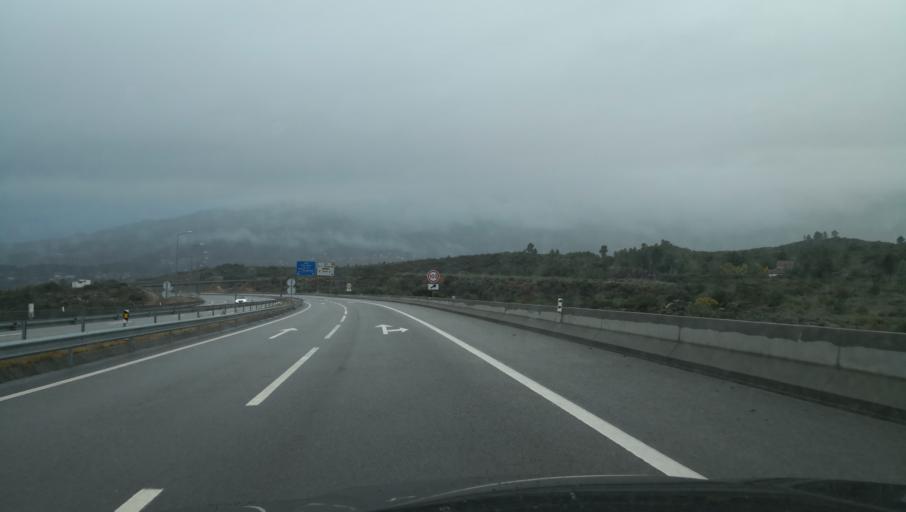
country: PT
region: Vila Real
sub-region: Vila Real
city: Vila Real
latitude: 41.3644
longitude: -7.6925
